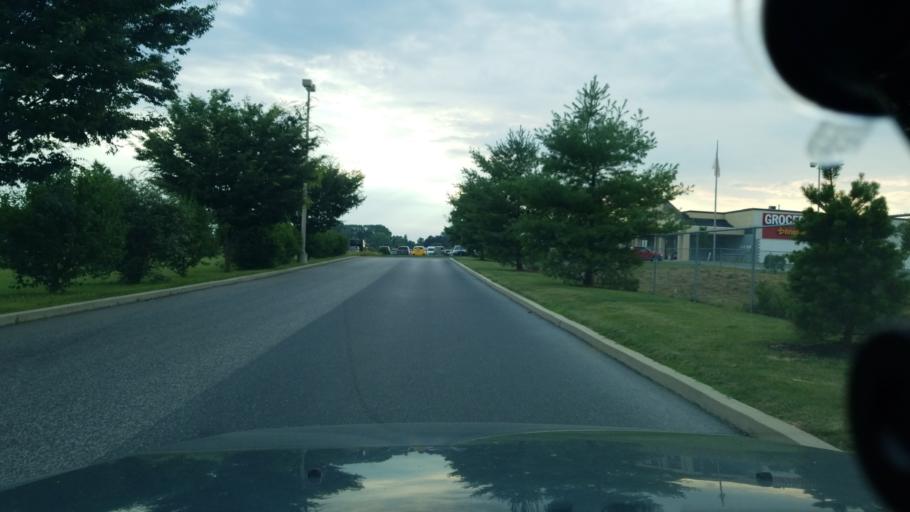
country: US
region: Pennsylvania
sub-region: Lebanon County
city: Palmyra
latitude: 40.3207
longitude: -76.5651
